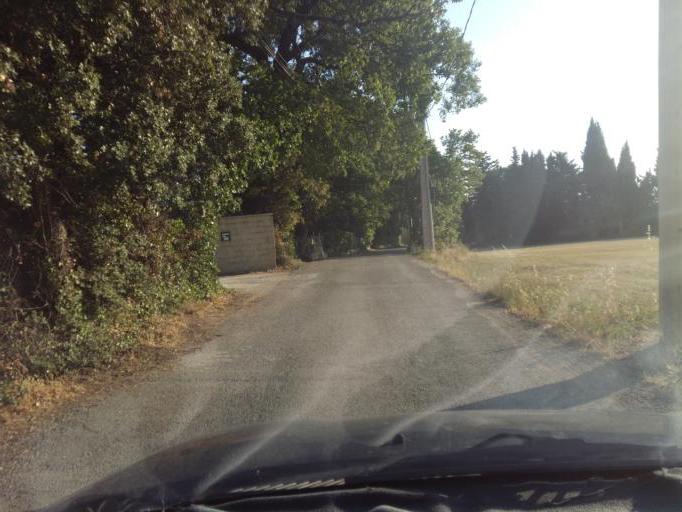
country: FR
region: Provence-Alpes-Cote d'Azur
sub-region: Departement du Vaucluse
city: Carpentras
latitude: 44.0718
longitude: 5.0624
